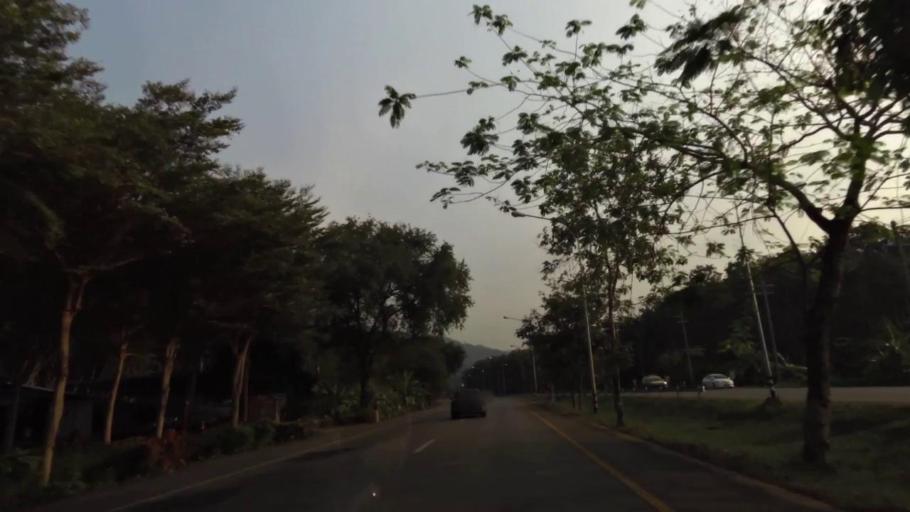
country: TH
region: Chanthaburi
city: Chanthaburi
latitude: 12.5776
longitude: 102.1600
